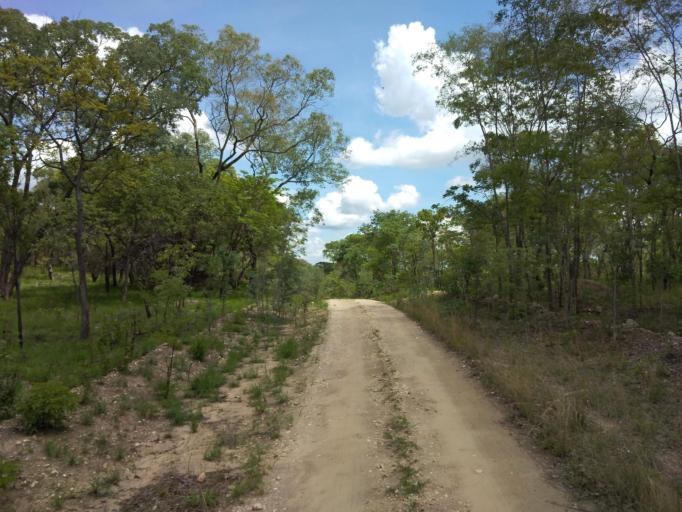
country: ZM
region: Central
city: Mkushi
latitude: -14.0822
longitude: 29.9735
